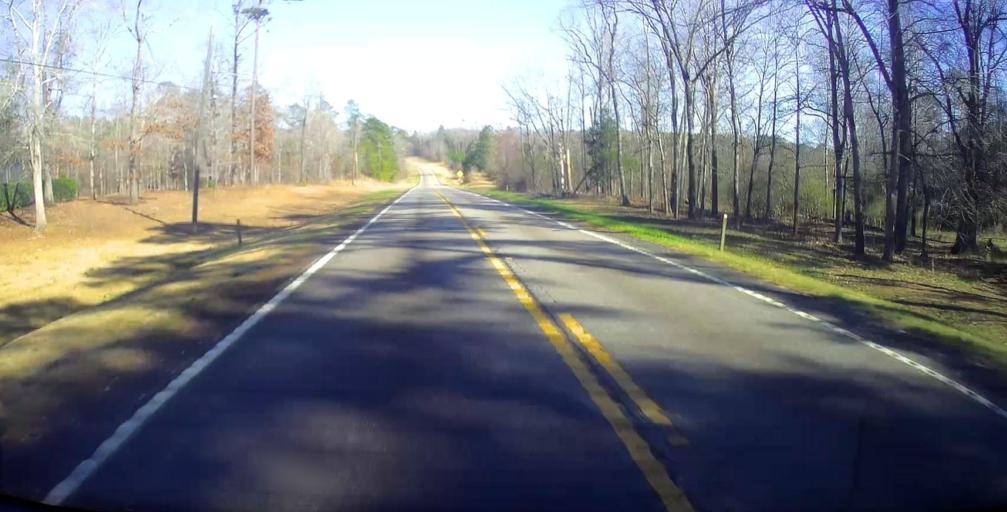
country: US
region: Georgia
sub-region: Schley County
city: Ellaville
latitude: 32.1820
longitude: -84.2564
